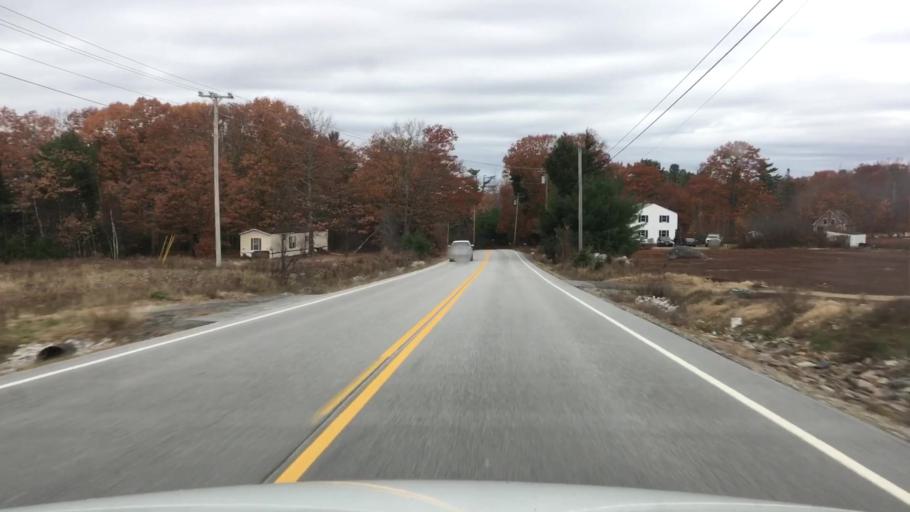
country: US
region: Maine
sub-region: Hancock County
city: Orland
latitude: 44.5536
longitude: -68.6941
